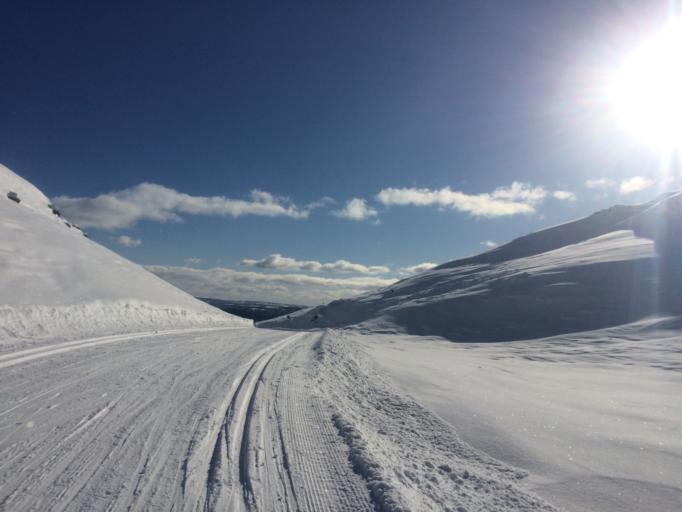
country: NO
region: Oppland
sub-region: Ringebu
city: Ringebu
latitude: 61.3774
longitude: 10.0593
